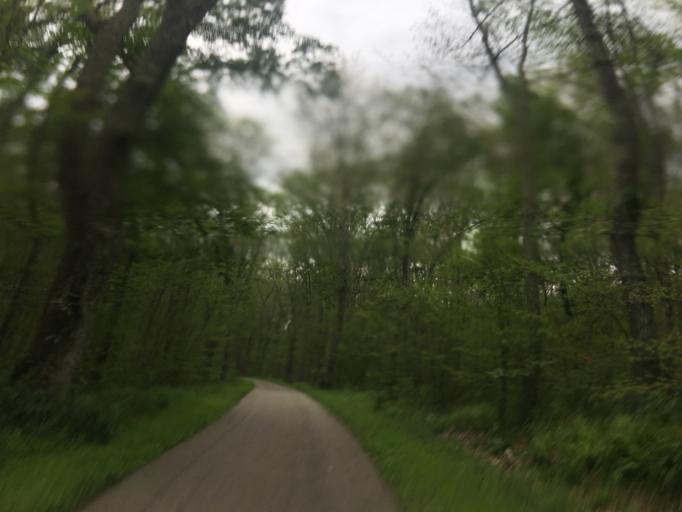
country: US
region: Connecticut
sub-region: Windham County
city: East Brooklyn
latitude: 41.7775
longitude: -71.9041
